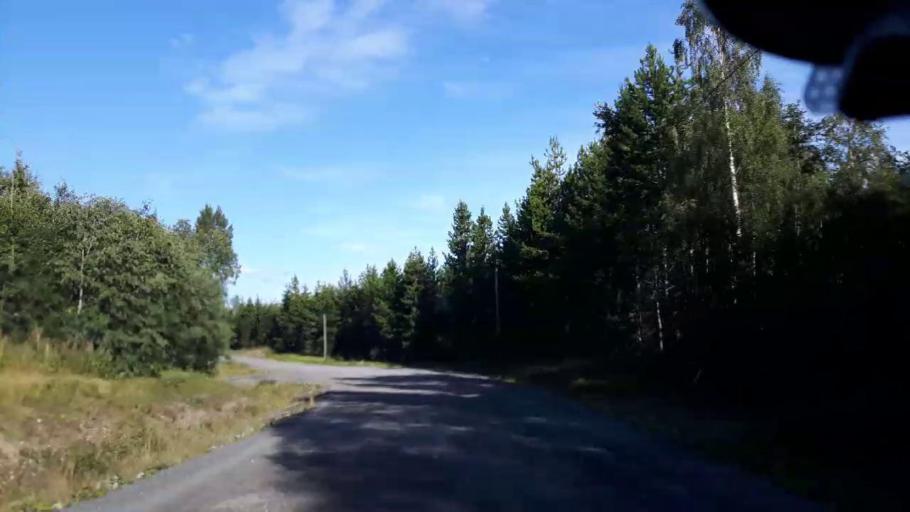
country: SE
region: Jaemtland
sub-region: Ragunda Kommun
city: Hammarstrand
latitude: 63.4436
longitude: 16.2101
